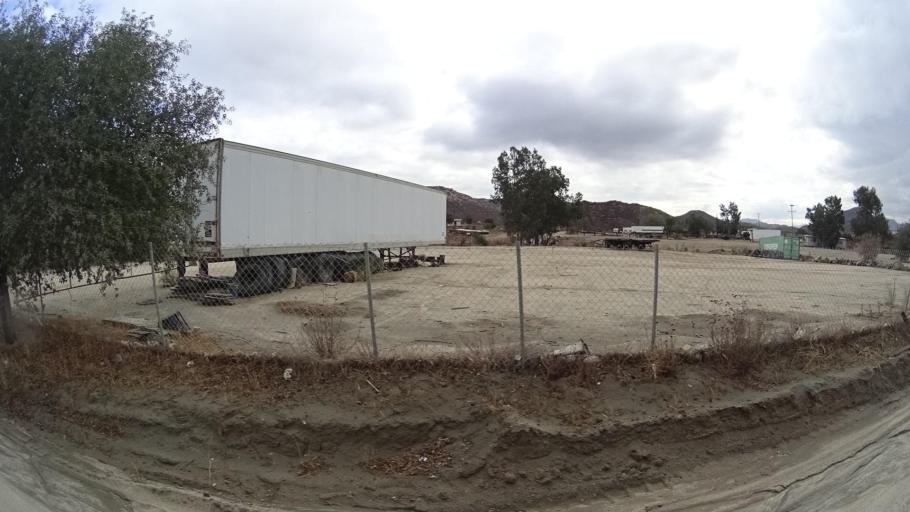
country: MX
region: Baja California
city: Tecate
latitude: 32.5876
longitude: -116.6208
